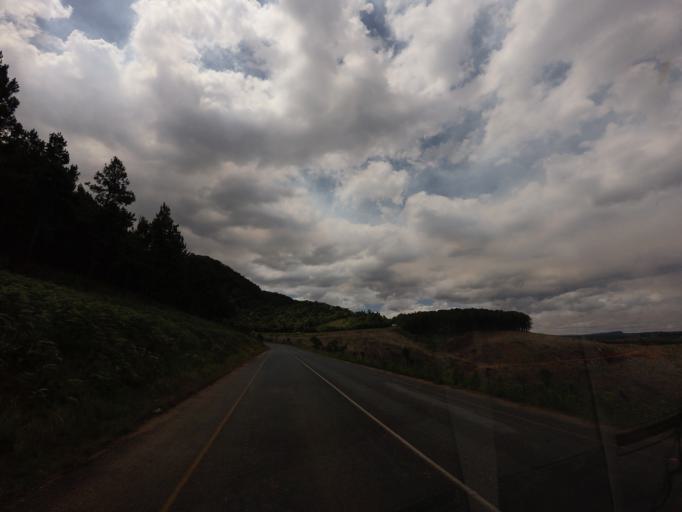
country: ZA
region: Mpumalanga
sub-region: Ehlanzeni District
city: Graksop
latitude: -24.9473
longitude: 30.8115
